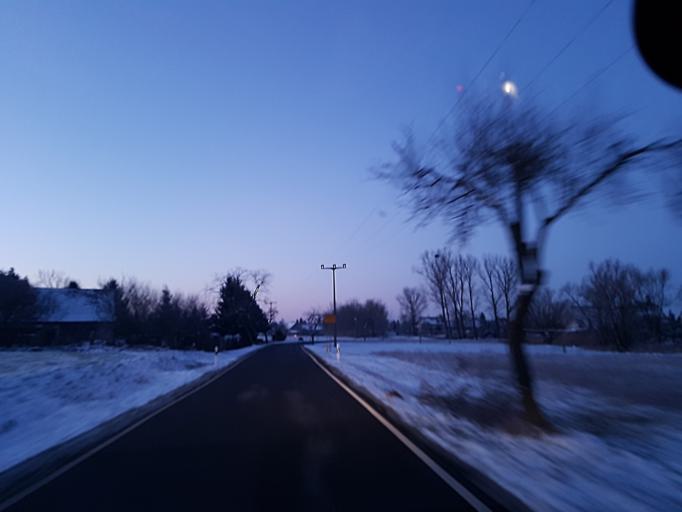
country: DE
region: Brandenburg
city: Muhlberg
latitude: 51.4777
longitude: 13.2716
